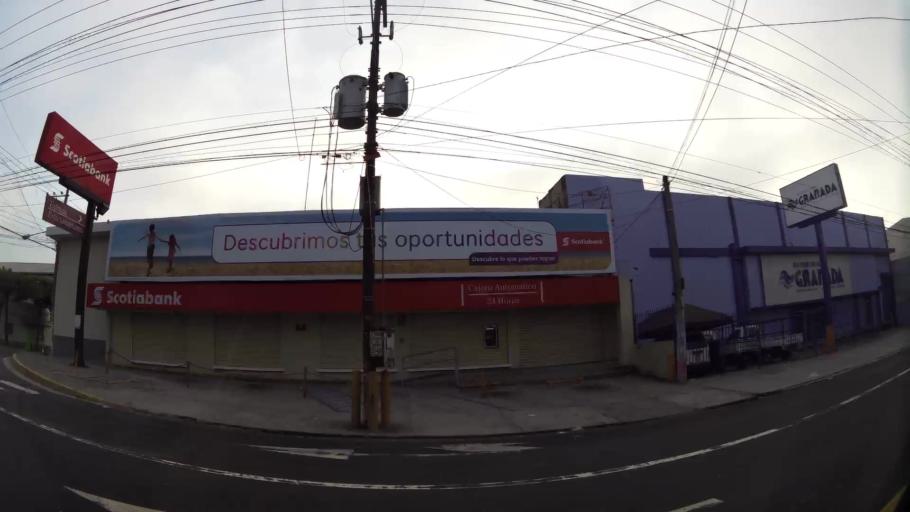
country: SV
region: San Salvador
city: San Salvador
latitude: 13.6943
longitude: -89.2055
